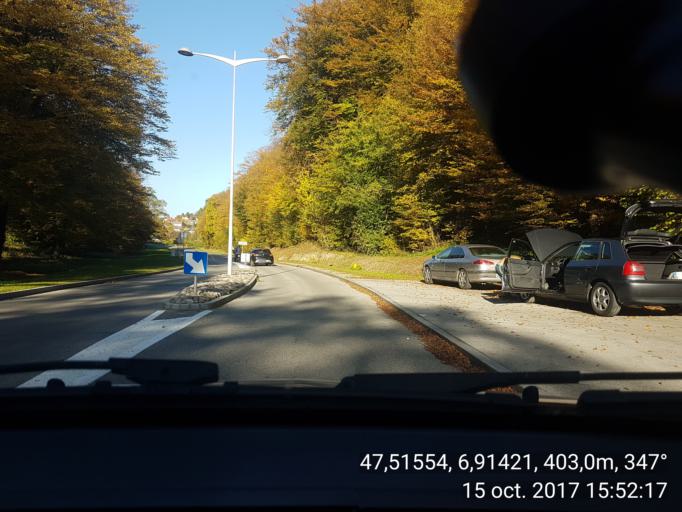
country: FR
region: Franche-Comte
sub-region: Departement du Doubs
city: Dampierre-les-Bois
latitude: 47.5155
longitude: 6.9141
